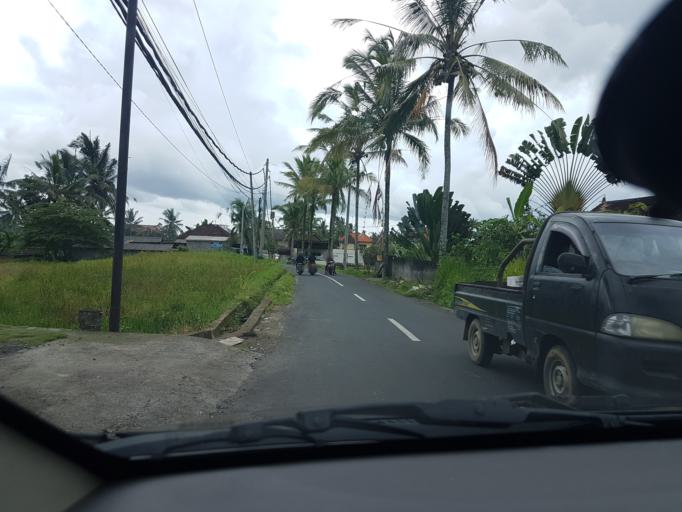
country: ID
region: Bali
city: Banjar Triwangsakeliki
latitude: -8.4659
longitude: 115.2724
